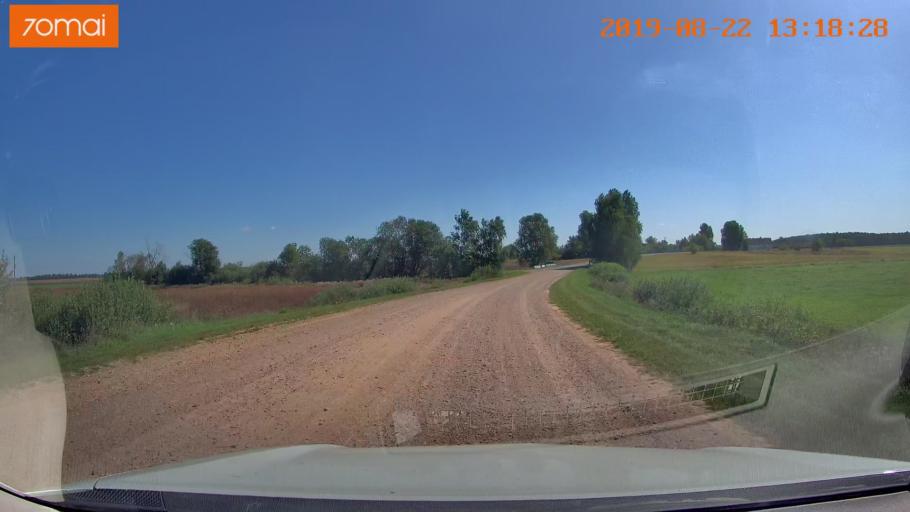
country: BY
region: Minsk
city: Urechcha
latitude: 53.2407
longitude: 27.9401
